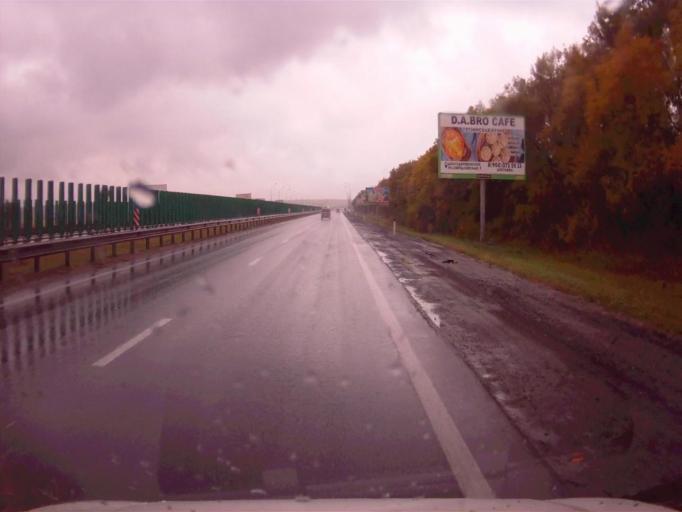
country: RU
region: Chelyabinsk
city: Dolgoderevenskoye
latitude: 55.3026
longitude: 61.3362
